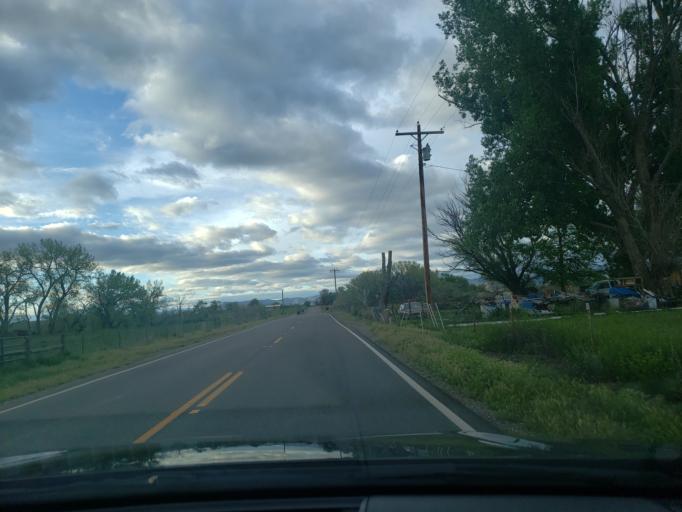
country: US
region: Colorado
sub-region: Mesa County
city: Fruita
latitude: 39.1955
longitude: -108.7289
